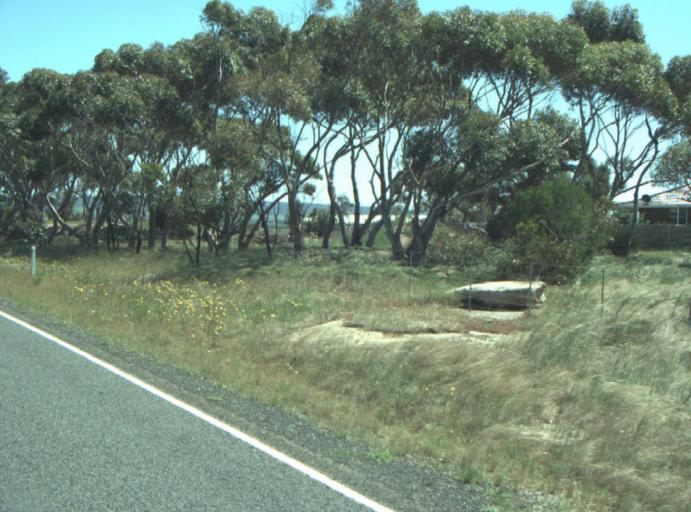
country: AU
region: Victoria
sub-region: Greater Geelong
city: Lara
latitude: -37.8873
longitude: 144.3433
